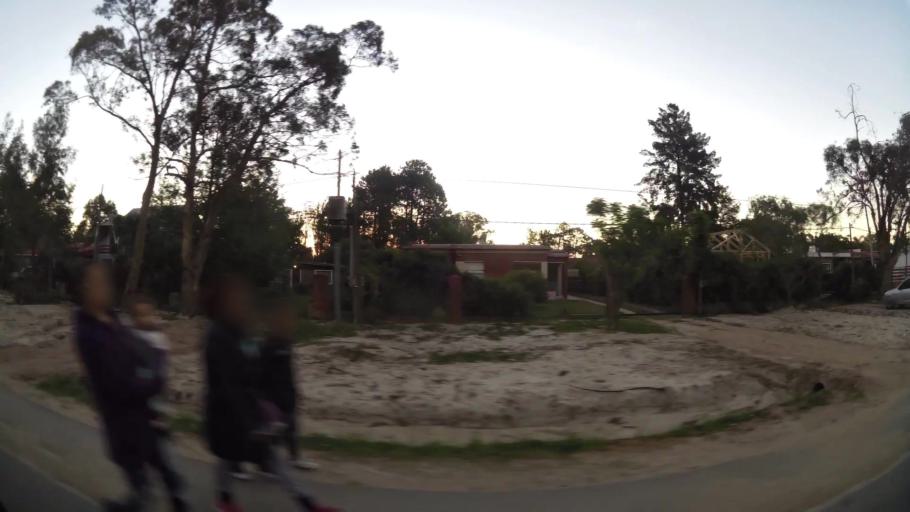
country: UY
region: Canelones
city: Colonia Nicolich
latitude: -34.8244
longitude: -55.9568
